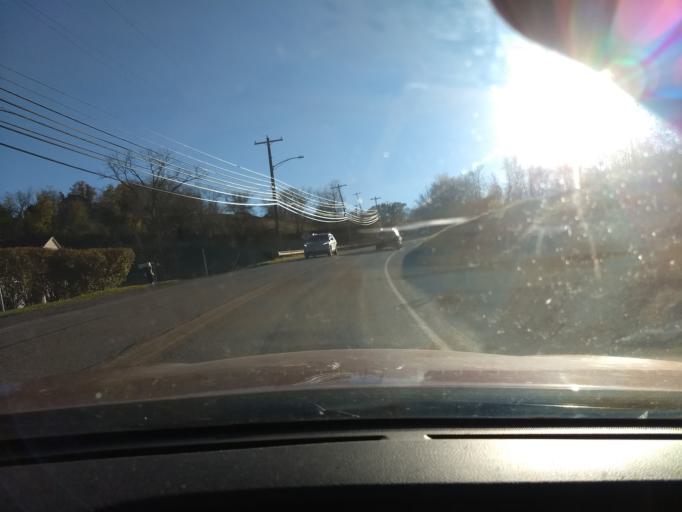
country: US
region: Pennsylvania
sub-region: Allegheny County
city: Oakdale
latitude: 40.3882
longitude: -80.1844
